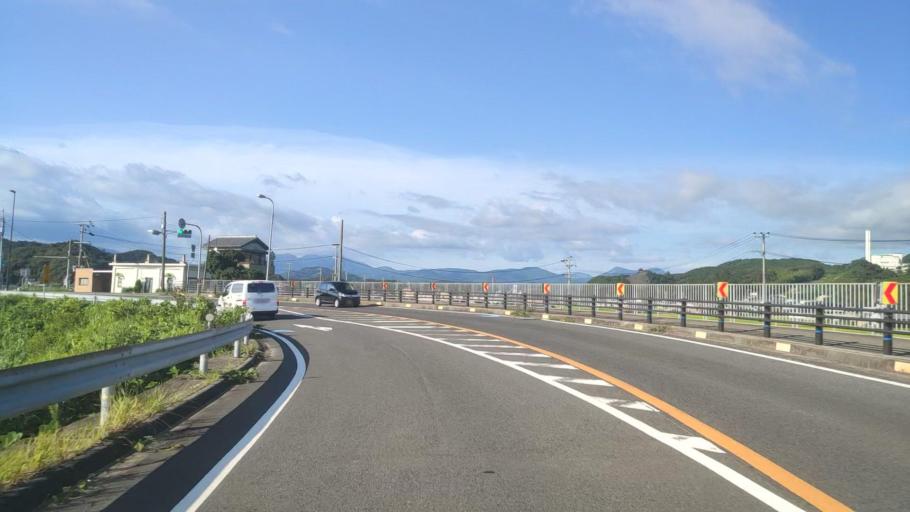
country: JP
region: Wakayama
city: Tanabe
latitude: 33.6790
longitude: 135.4095
